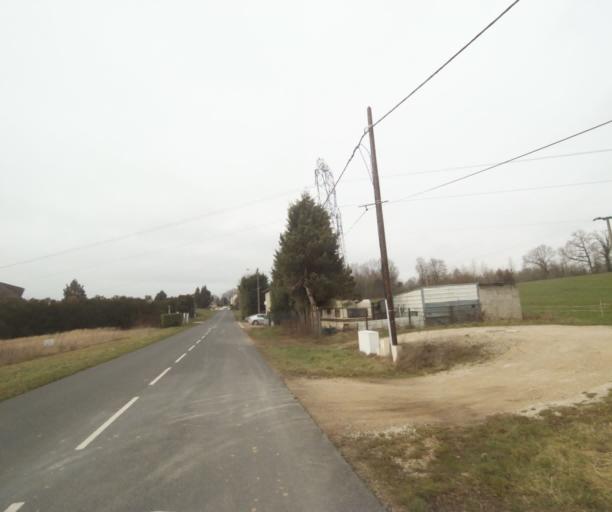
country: FR
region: Champagne-Ardenne
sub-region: Departement de la Marne
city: Pargny-sur-Saulx
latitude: 48.7483
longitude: 4.8595
